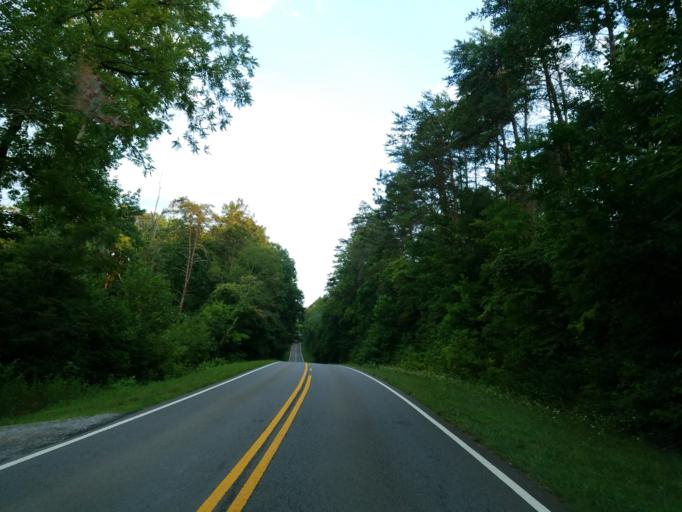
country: US
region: Georgia
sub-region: Pickens County
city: Jasper
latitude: 34.5271
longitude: -84.4764
